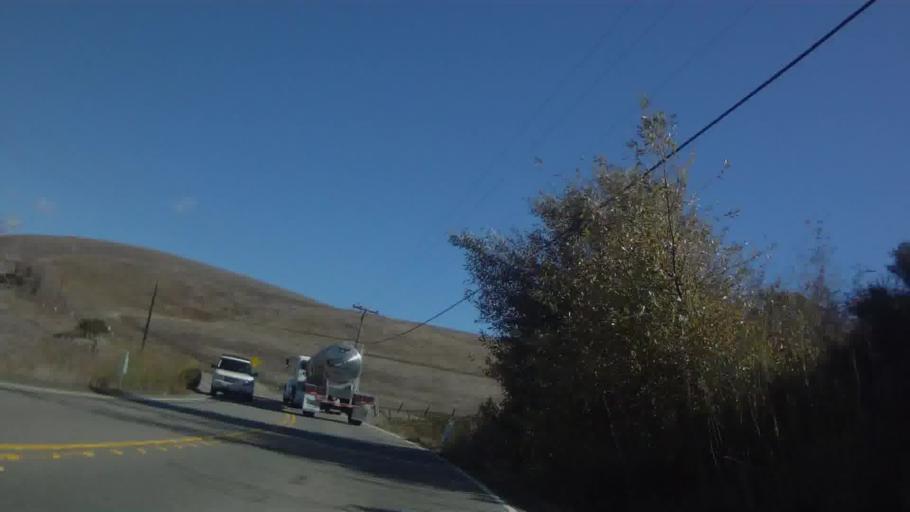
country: US
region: California
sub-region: Sonoma County
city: Temelec
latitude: 38.2165
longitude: -122.5456
